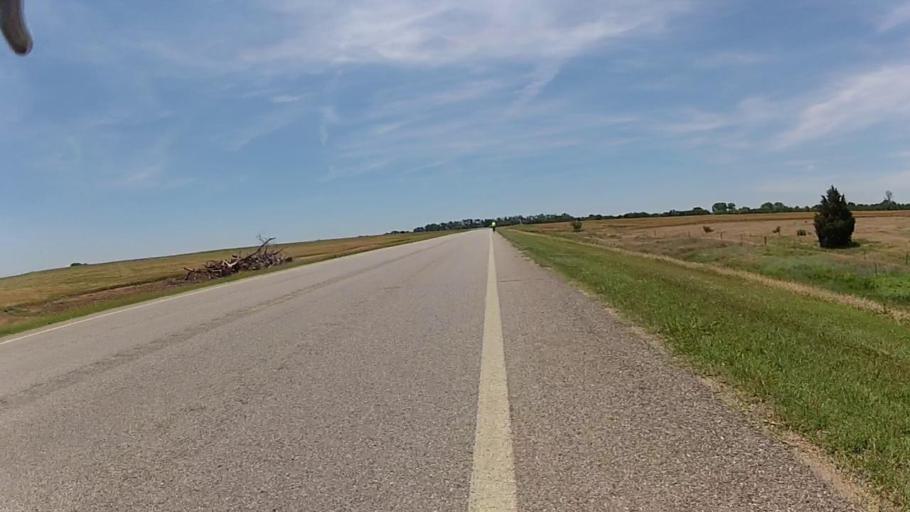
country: US
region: Kansas
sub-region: Barber County
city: Medicine Lodge
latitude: 37.2599
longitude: -98.5272
